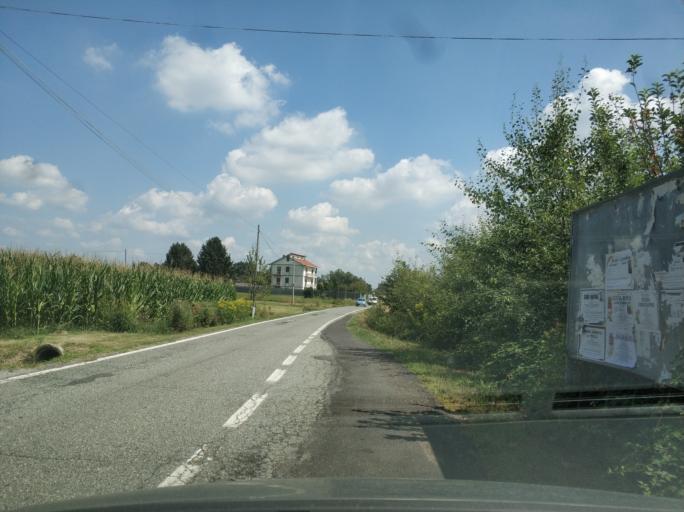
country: IT
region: Piedmont
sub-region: Provincia di Torino
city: San Francesco al Campo
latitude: 45.2502
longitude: 7.6701
